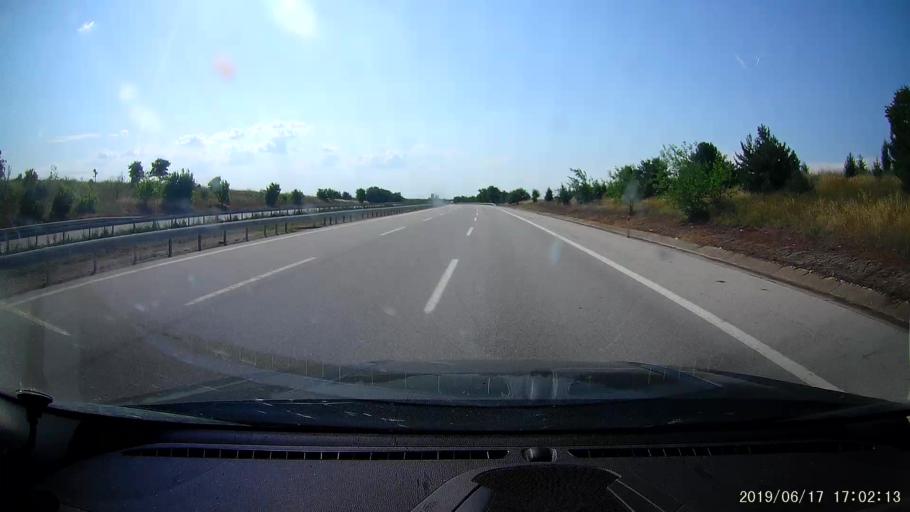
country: TR
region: Edirne
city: Haskoy
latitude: 41.6377
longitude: 26.7866
